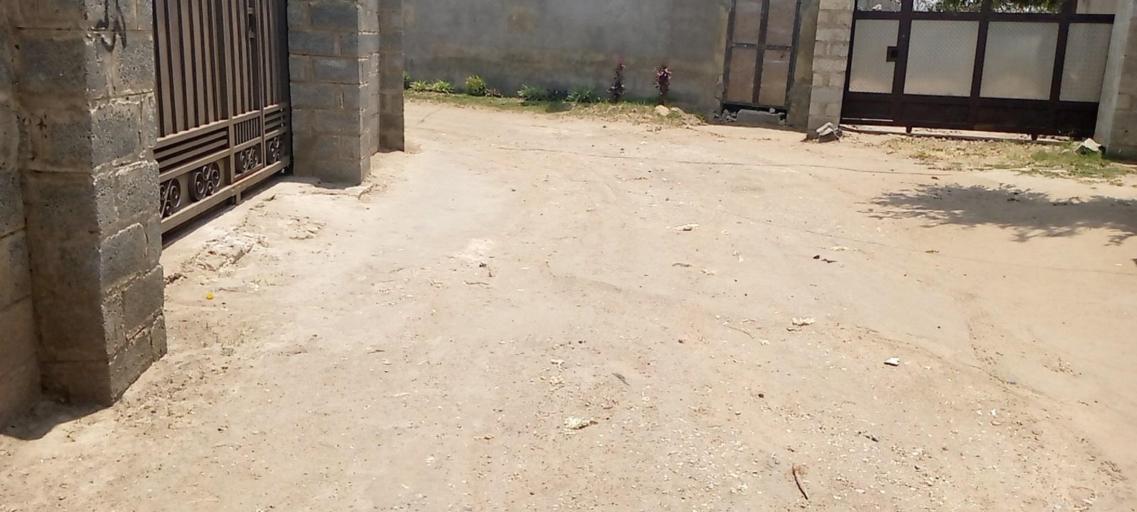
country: ZM
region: Lusaka
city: Lusaka
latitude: -15.4001
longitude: 28.3453
